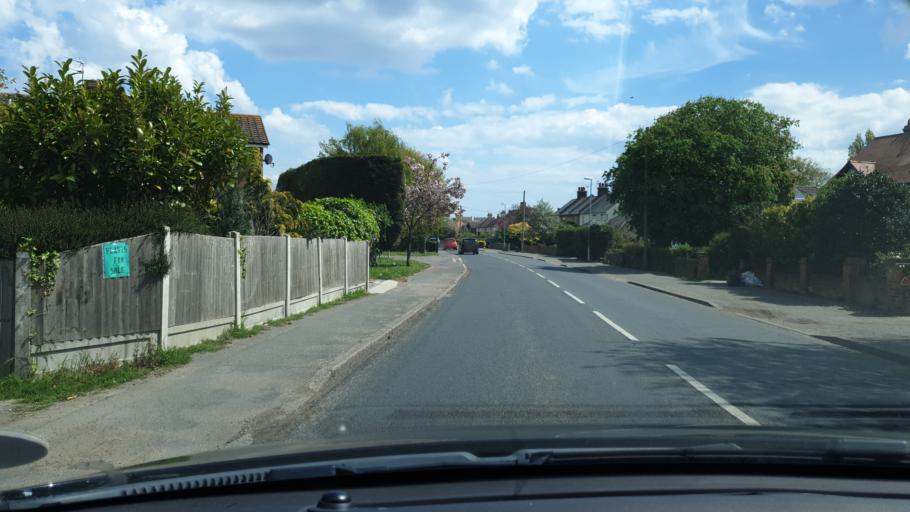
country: GB
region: England
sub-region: Essex
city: Walton-on-the-Naze
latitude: 51.8493
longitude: 1.2592
